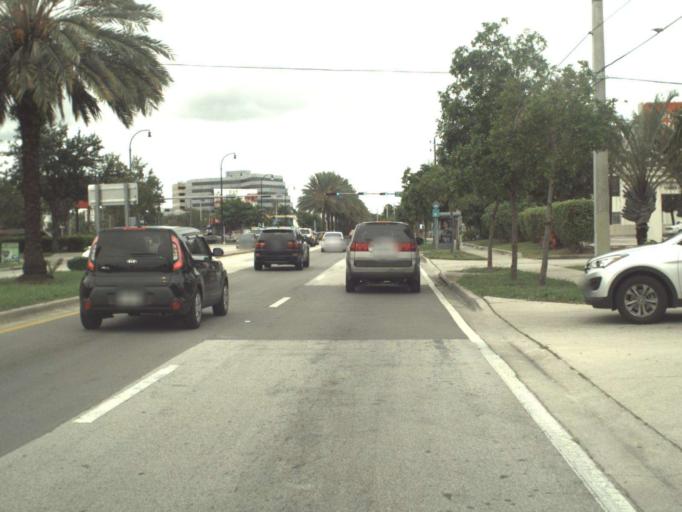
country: US
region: Florida
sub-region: Miami-Dade County
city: Biscayne Park
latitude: 25.8816
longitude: -80.1664
